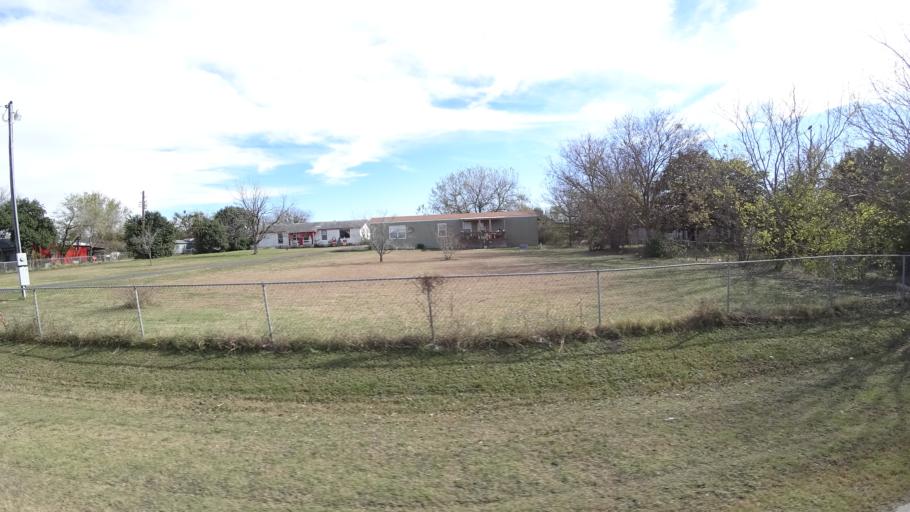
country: US
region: Texas
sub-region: Travis County
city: Onion Creek
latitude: 30.1268
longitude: -97.7391
